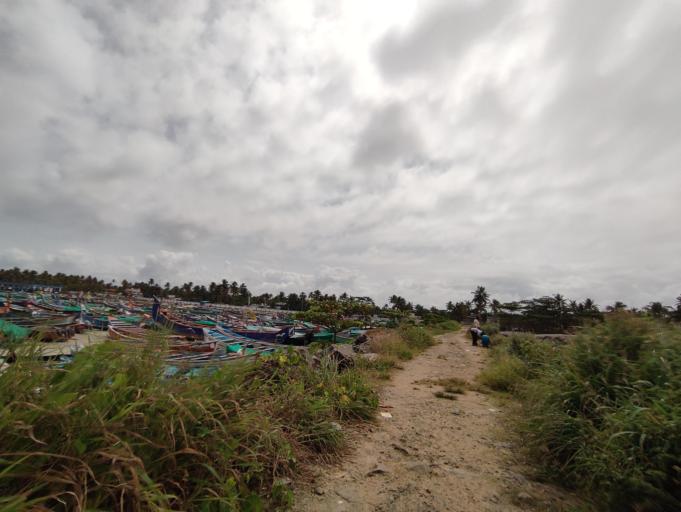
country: IN
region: Kerala
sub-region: Alappuzha
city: Kutiatodu
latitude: 9.7983
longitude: 76.2742
